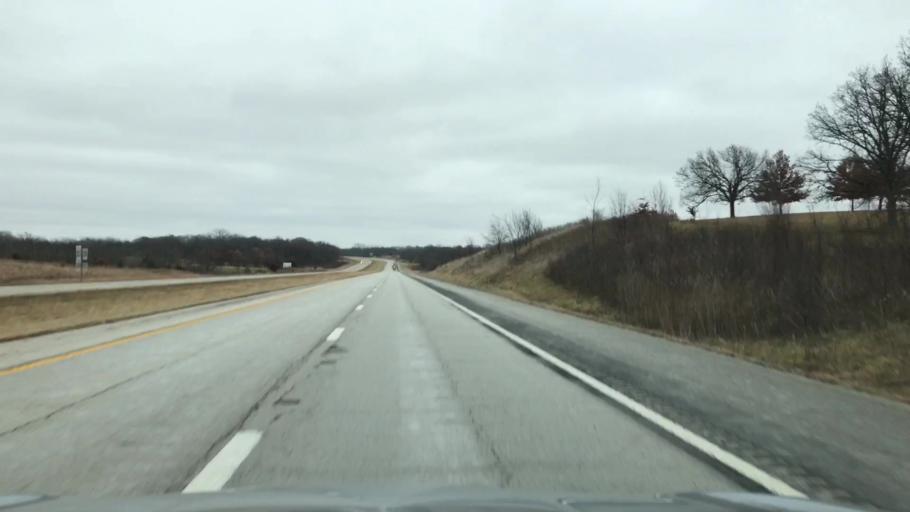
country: US
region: Missouri
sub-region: Caldwell County
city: Hamilton
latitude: 39.7406
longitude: -94.0363
